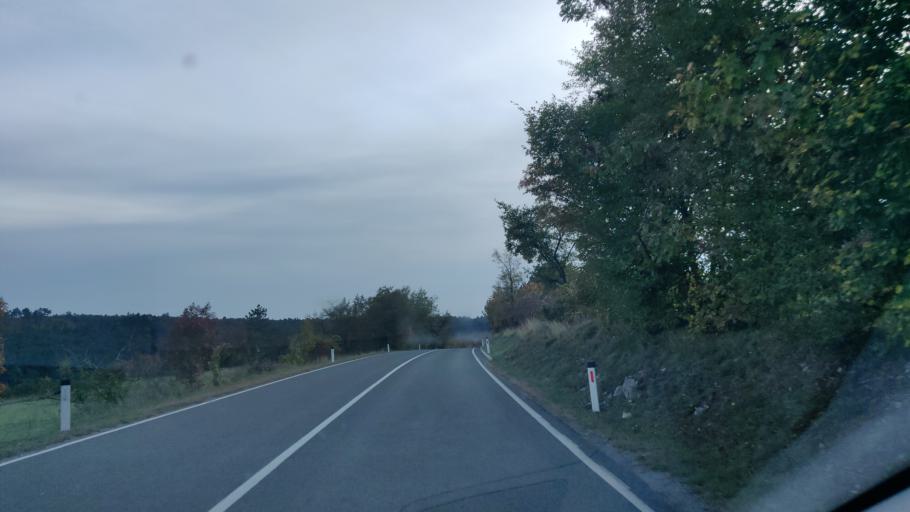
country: SI
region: Ajdovscina
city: Lokavec
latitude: 45.8121
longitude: 13.8494
